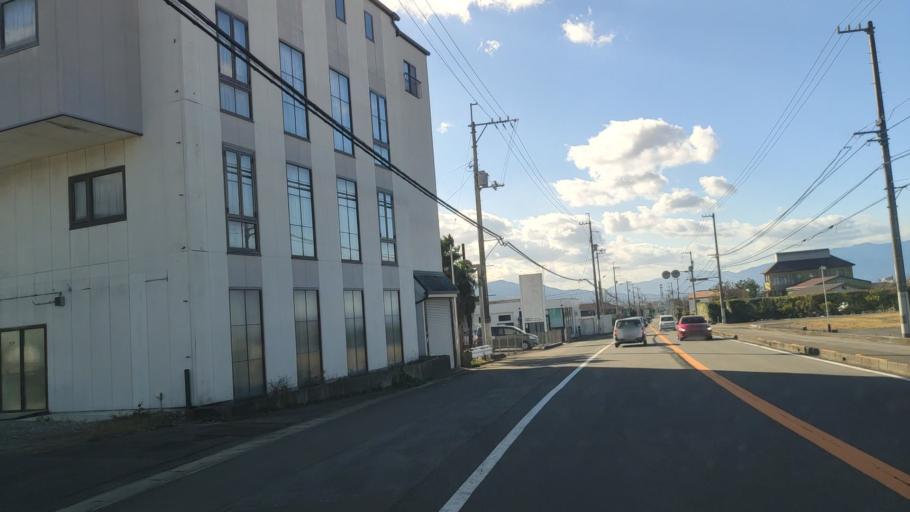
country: JP
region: Ehime
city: Saijo
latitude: 33.9156
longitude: 133.2171
